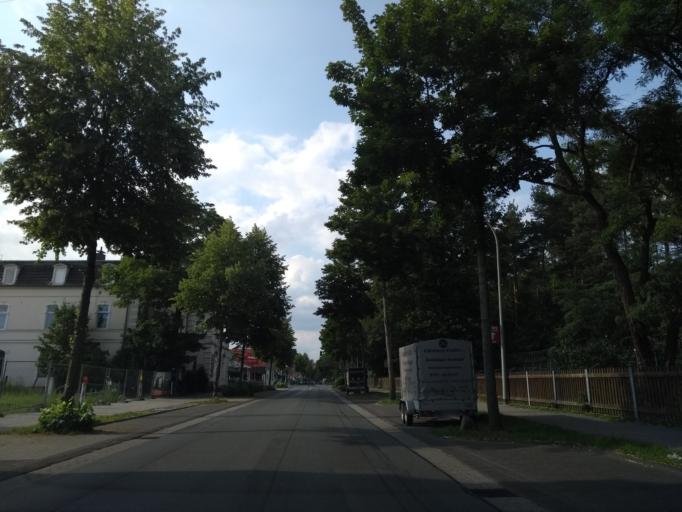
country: DE
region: North Rhine-Westphalia
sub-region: Regierungsbezirk Detmold
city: Paderborn
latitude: 51.7690
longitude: 8.7166
